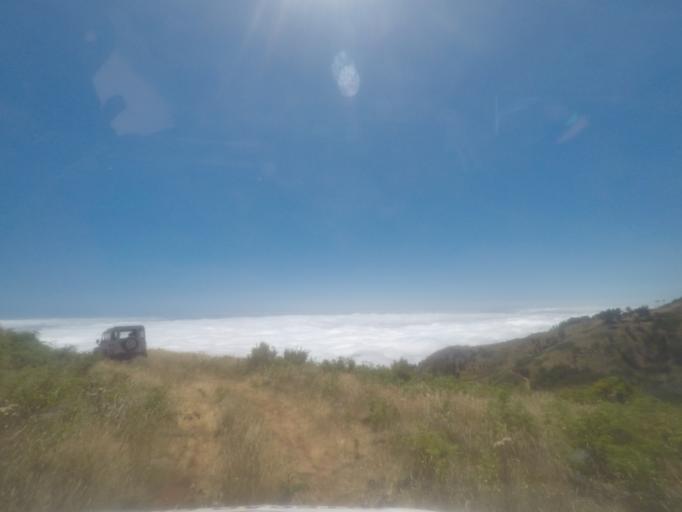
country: PT
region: Madeira
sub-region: Funchal
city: Nossa Senhora do Monte
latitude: 32.7082
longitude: -16.8975
